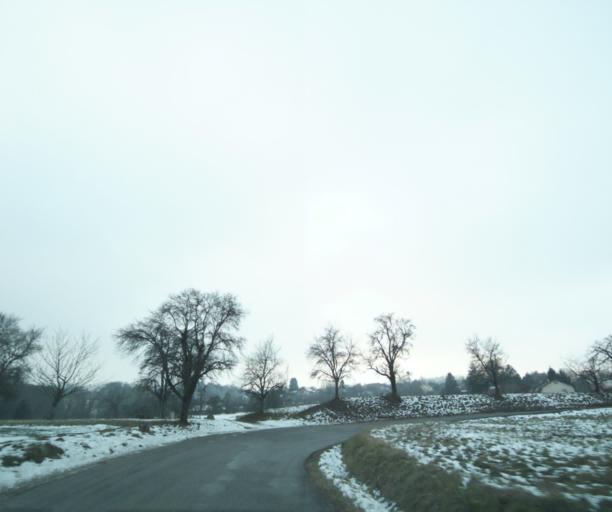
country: FR
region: Rhone-Alpes
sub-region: Departement de la Haute-Savoie
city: Reignier-Esery
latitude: 46.1259
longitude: 6.2585
